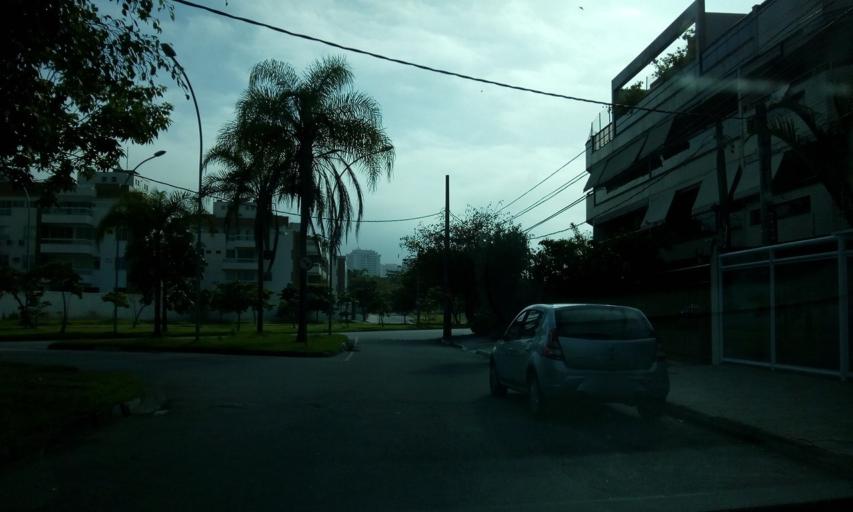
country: BR
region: Rio de Janeiro
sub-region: Nilopolis
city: Nilopolis
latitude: -23.0125
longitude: -43.4492
